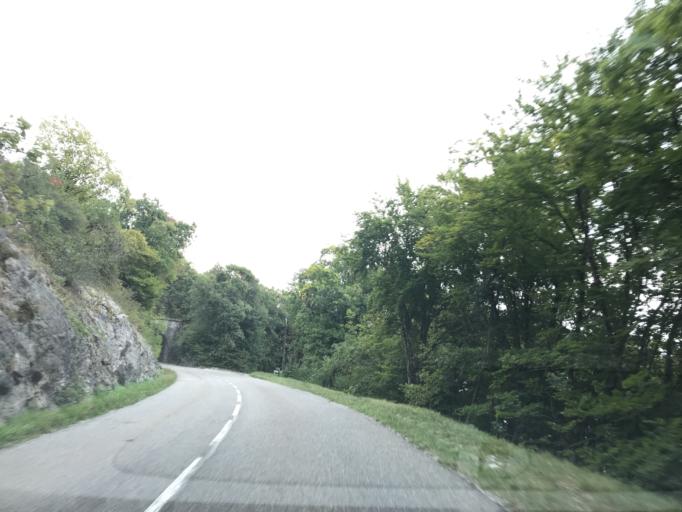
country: FR
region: Rhone-Alpes
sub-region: Departement de la Haute-Savoie
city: Talloires
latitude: 45.8475
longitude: 6.2198
